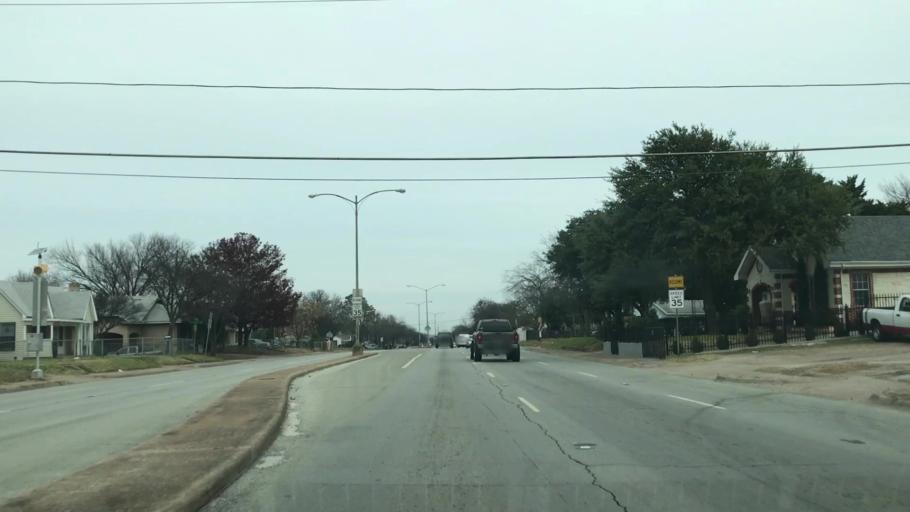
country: US
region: Texas
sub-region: Dallas County
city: Dallas
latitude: 32.7232
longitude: -96.8145
